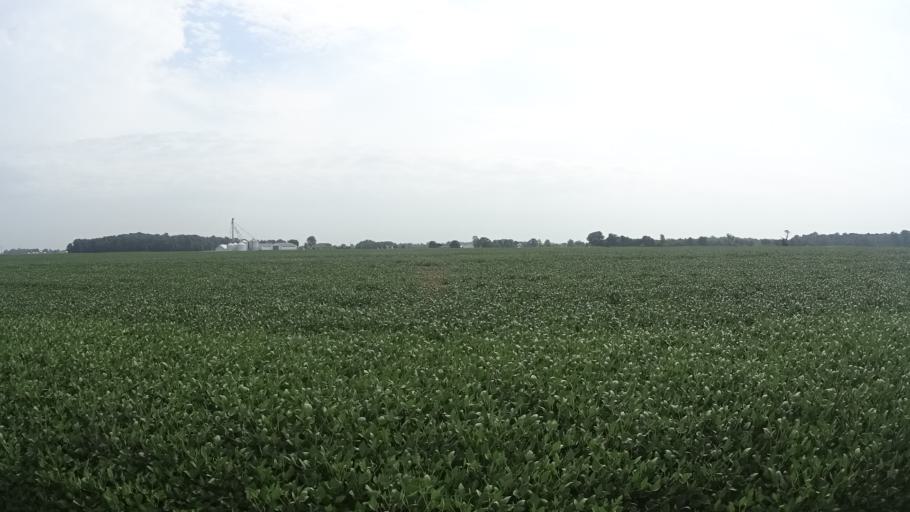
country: US
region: Indiana
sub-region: Madison County
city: Pendleton
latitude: 40.0261
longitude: -85.7915
